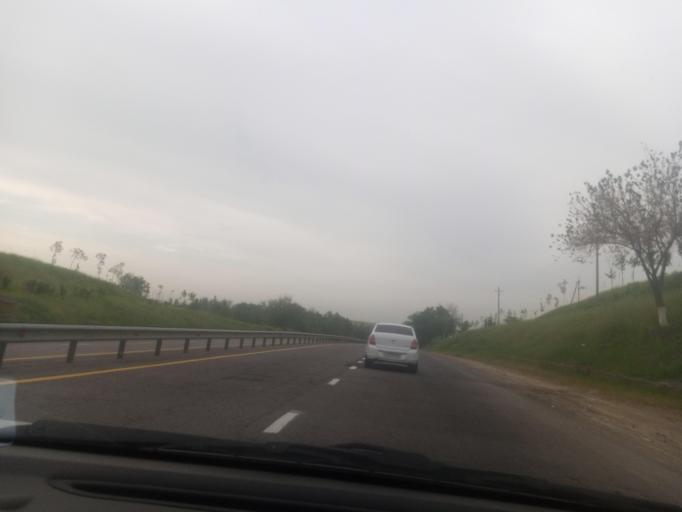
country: UZ
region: Toshkent
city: Tuytepa
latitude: 41.0829
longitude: 69.4683
